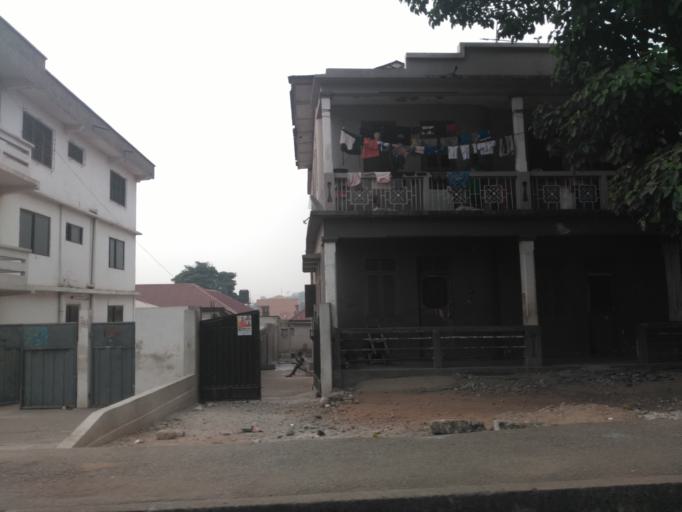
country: GH
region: Ashanti
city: Tafo
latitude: 6.7082
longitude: -1.6054
